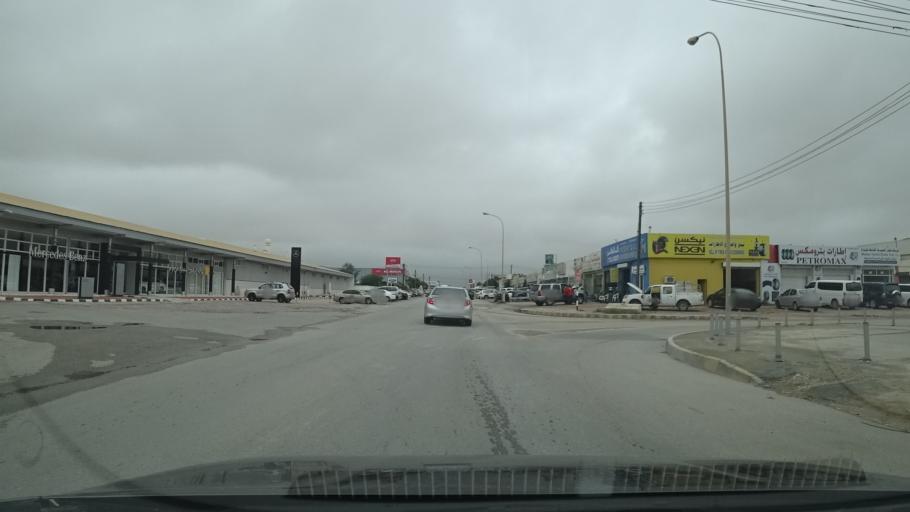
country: OM
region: Zufar
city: Salalah
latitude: 17.0137
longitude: 54.0465
